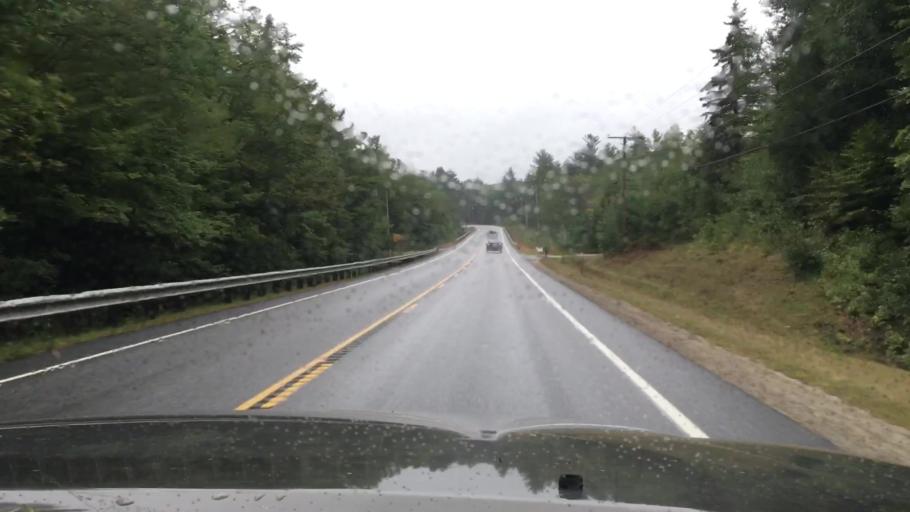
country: US
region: New Hampshire
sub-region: Cheshire County
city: Harrisville
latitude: 43.0516
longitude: -72.0778
